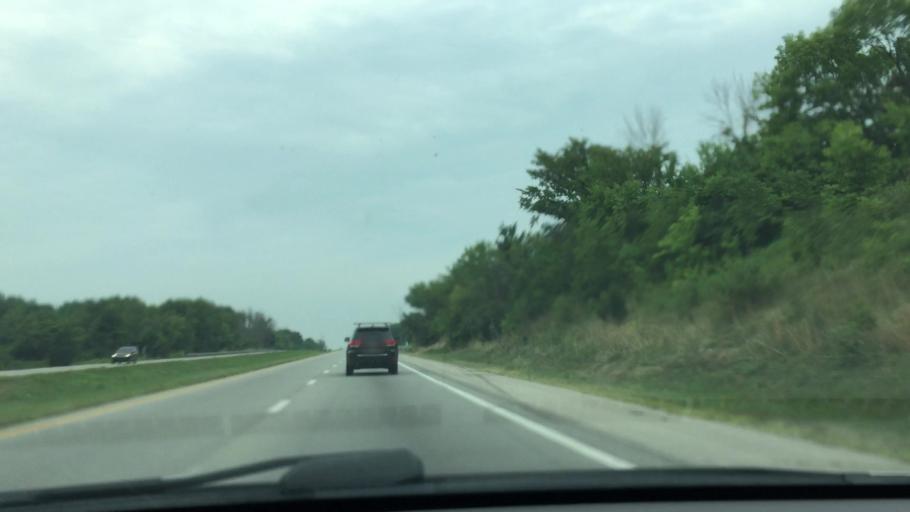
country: US
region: Kentucky
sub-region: Trimble County
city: Providence
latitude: 38.5506
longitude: -85.2065
